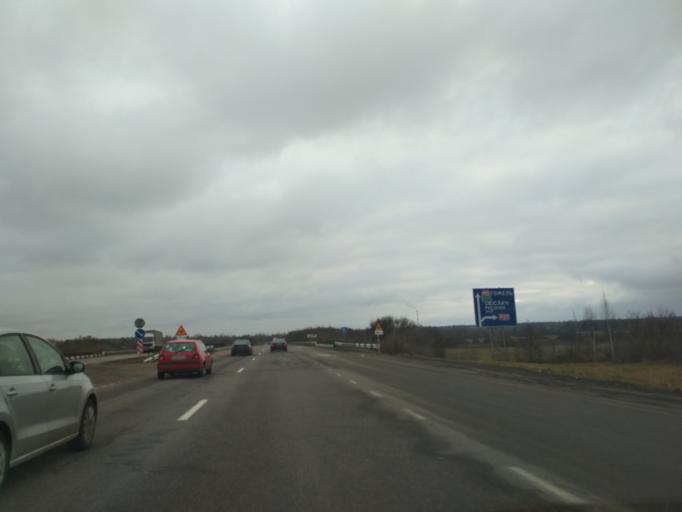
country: BY
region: Minsk
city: Dukora
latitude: 53.6681
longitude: 27.9365
